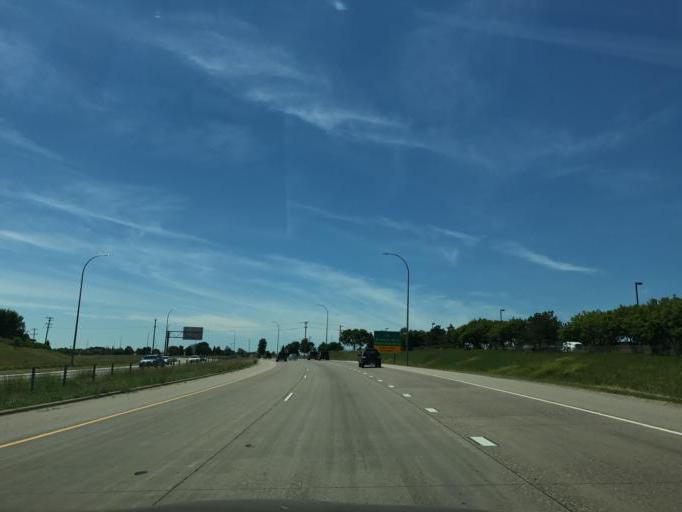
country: US
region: Minnesota
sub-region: Hennepin County
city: Osseo
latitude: 45.1033
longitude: -93.3977
